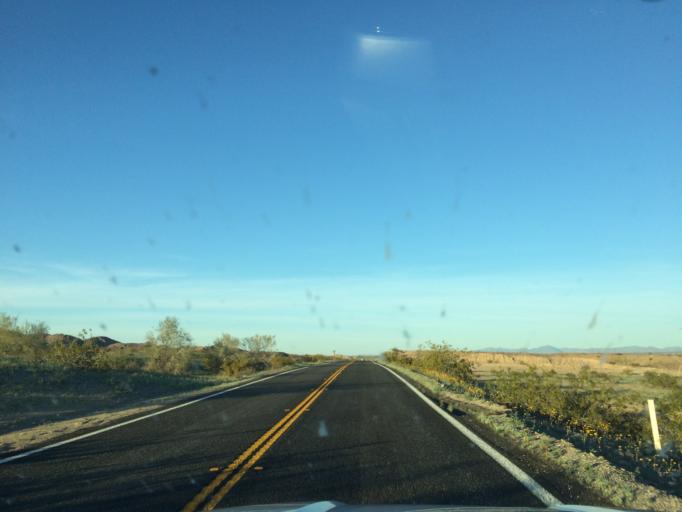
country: US
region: California
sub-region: Riverside County
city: Mesa Verde
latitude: 33.3079
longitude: -114.7407
